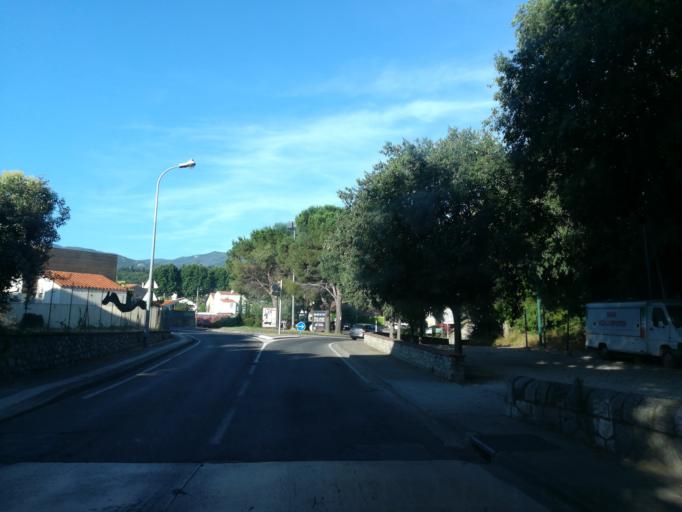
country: FR
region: Languedoc-Roussillon
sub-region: Departement des Pyrenees-Orientales
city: Ceret
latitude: 42.4949
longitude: 2.7426
